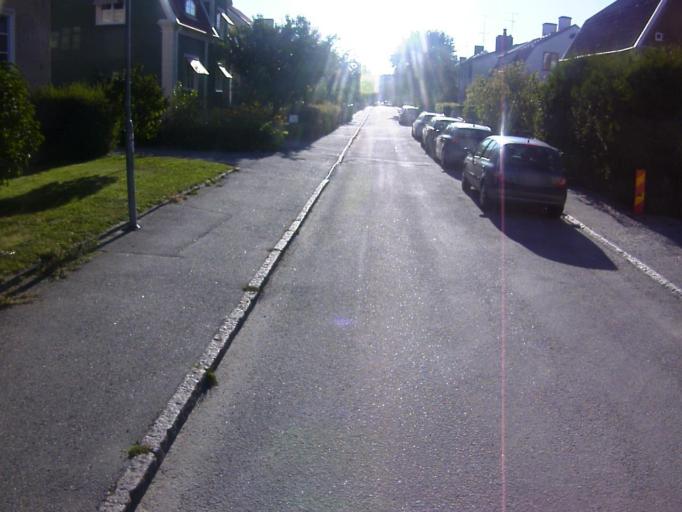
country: SE
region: Soedermanland
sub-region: Eskilstuna Kommun
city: Eskilstuna
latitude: 59.3699
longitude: 16.5238
